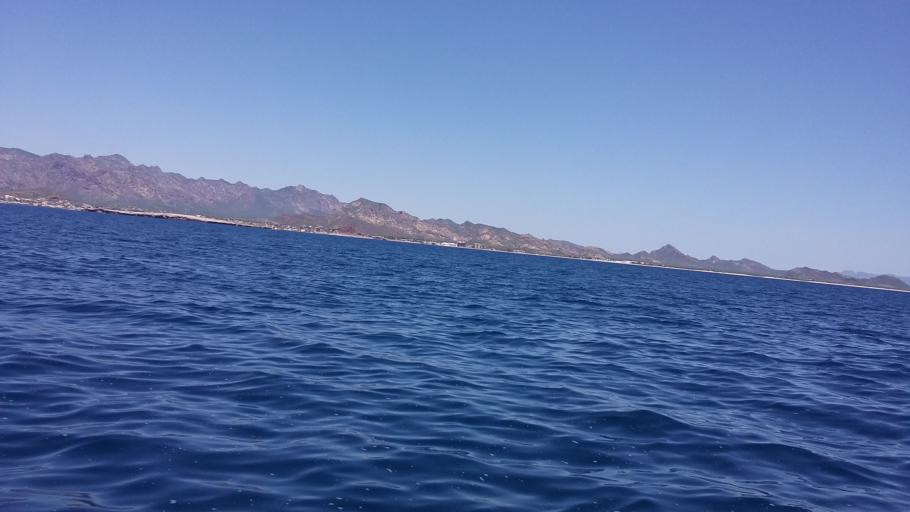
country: MX
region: Sonora
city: Heroica Guaymas
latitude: 27.9290
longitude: -111.0233
